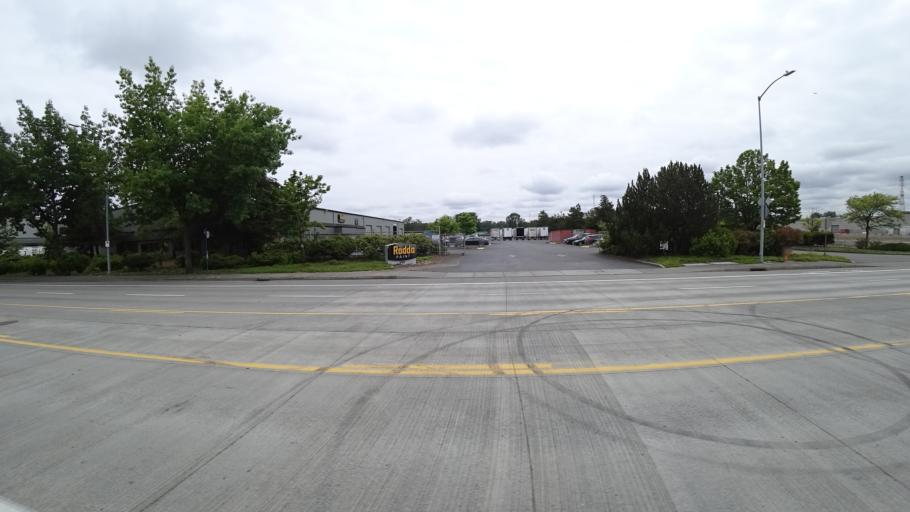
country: US
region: Washington
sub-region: Clark County
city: Vancouver
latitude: 45.6249
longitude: -122.7357
